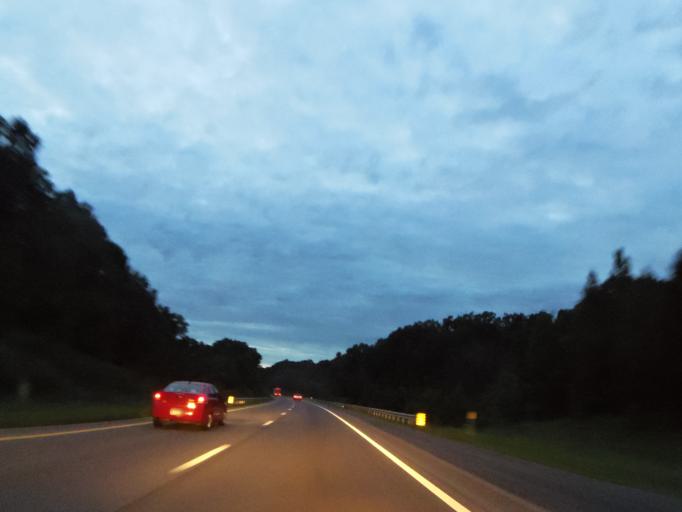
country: US
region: Tennessee
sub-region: Robertson County
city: Coopertown
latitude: 36.3622
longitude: -86.9491
